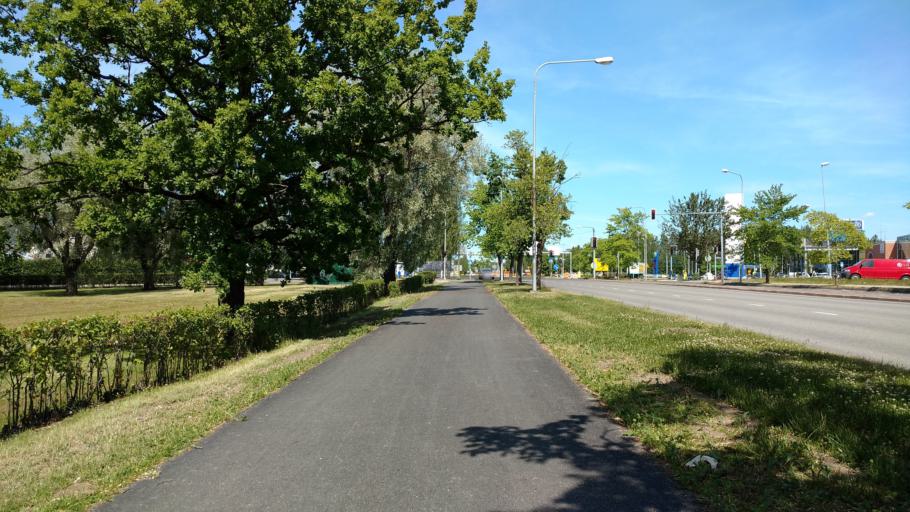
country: FI
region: Varsinais-Suomi
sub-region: Salo
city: Salo
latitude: 60.3919
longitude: 23.1292
